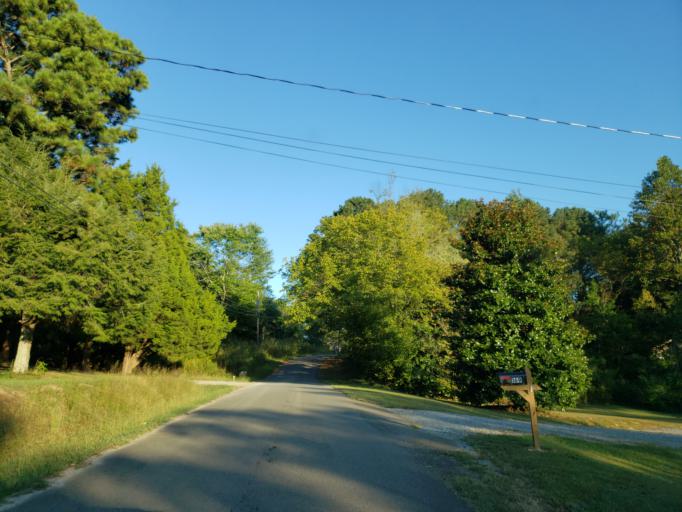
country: US
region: Georgia
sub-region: Pickens County
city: Jasper
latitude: 34.4554
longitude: -84.4452
